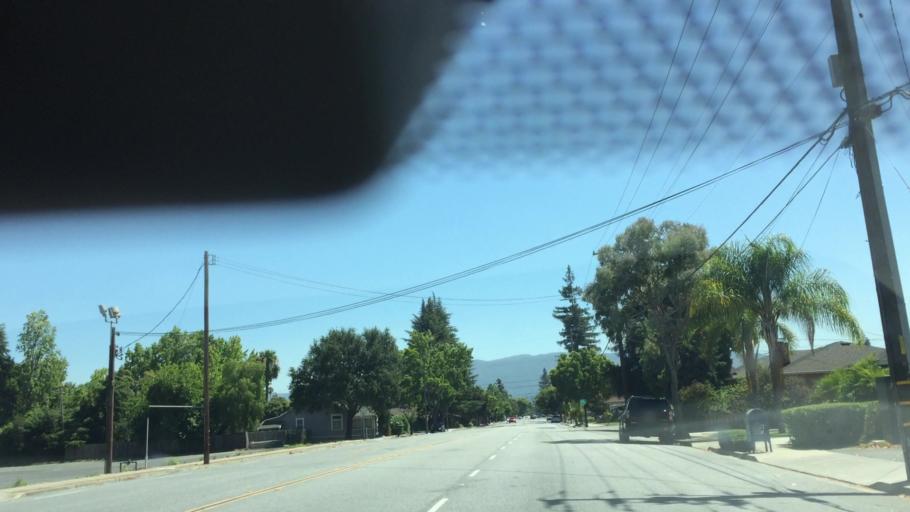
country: US
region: California
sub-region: Santa Clara County
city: Campbell
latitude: 37.2935
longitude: -121.9227
